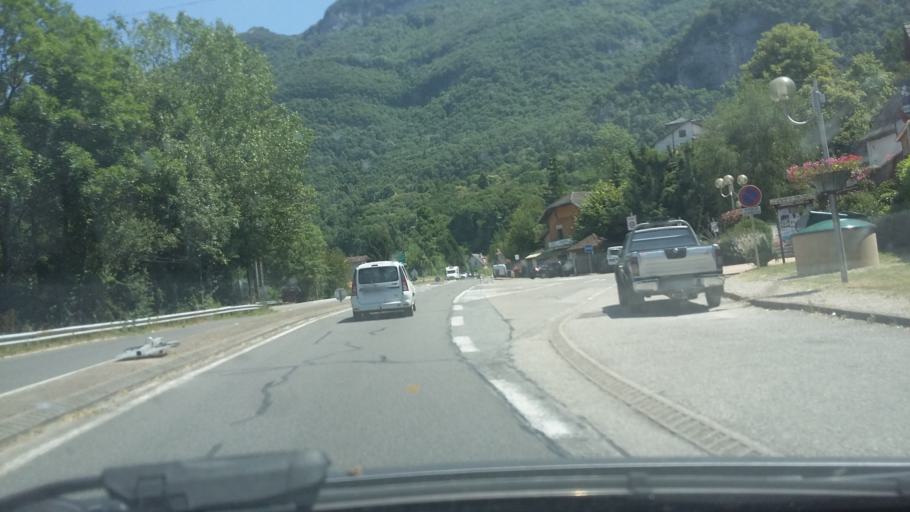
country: FR
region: Rhone-Alpes
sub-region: Departement de la Savoie
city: Le Bourget-du-Lac
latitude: 45.6905
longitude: 5.8194
